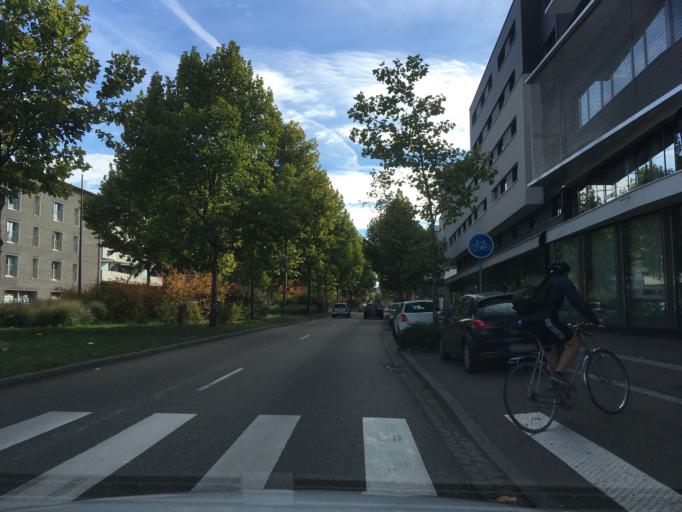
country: FR
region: Alsace
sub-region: Departement du Bas-Rhin
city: Strasbourg
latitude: 48.5724
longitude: 7.7660
